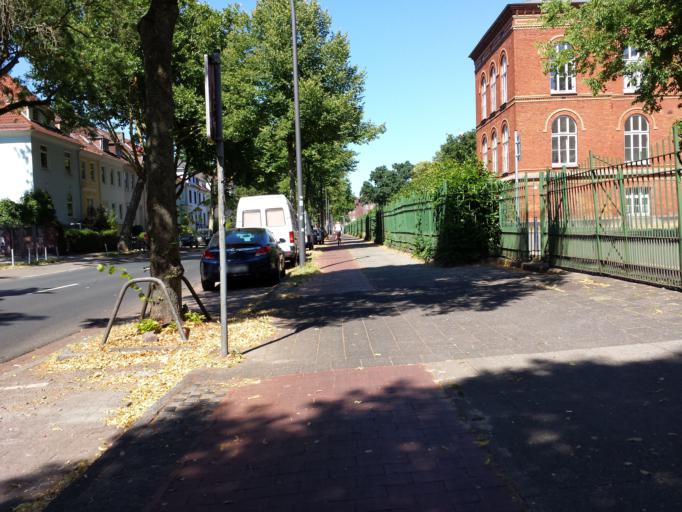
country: DE
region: Bremen
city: Bremen
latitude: 53.0724
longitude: 8.8347
